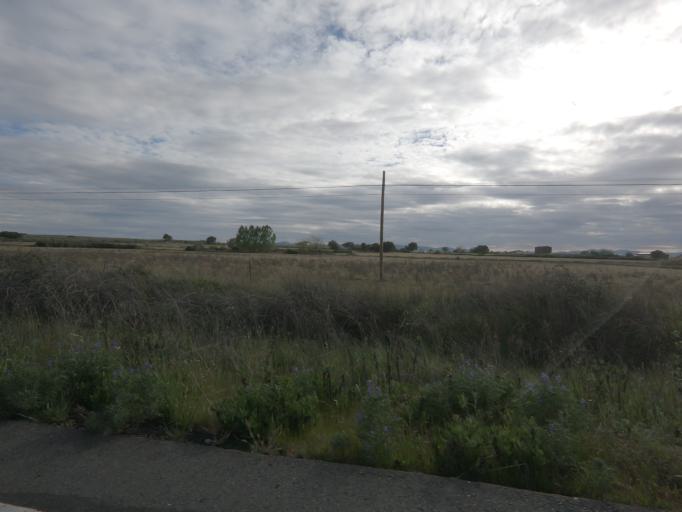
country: ES
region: Extremadura
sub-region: Provincia de Caceres
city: Moraleja
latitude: 40.0556
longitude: -6.6442
